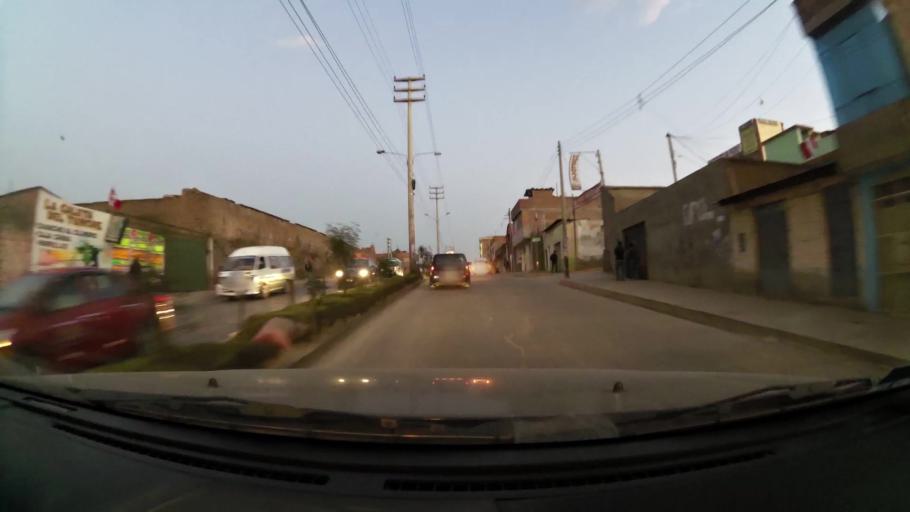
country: PE
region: Junin
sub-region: Provincia de Huancayo
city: El Tambo
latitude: -12.0600
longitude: -75.2210
